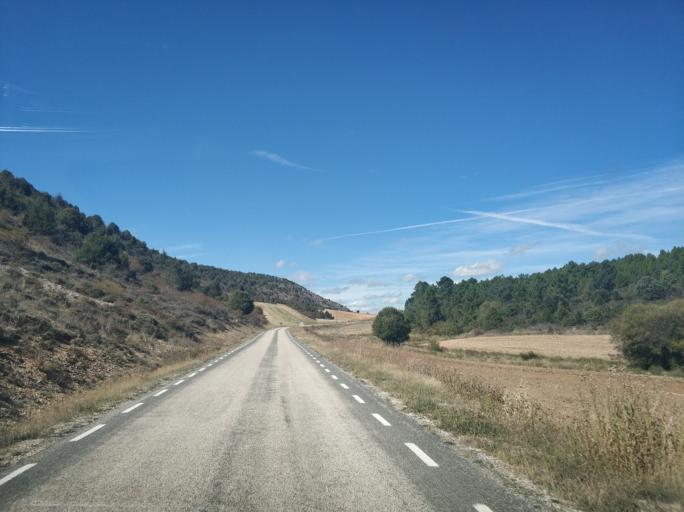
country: ES
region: Castille and Leon
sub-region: Provincia de Soria
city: Espeja de San Marcelino
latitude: 41.8162
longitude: -3.2345
